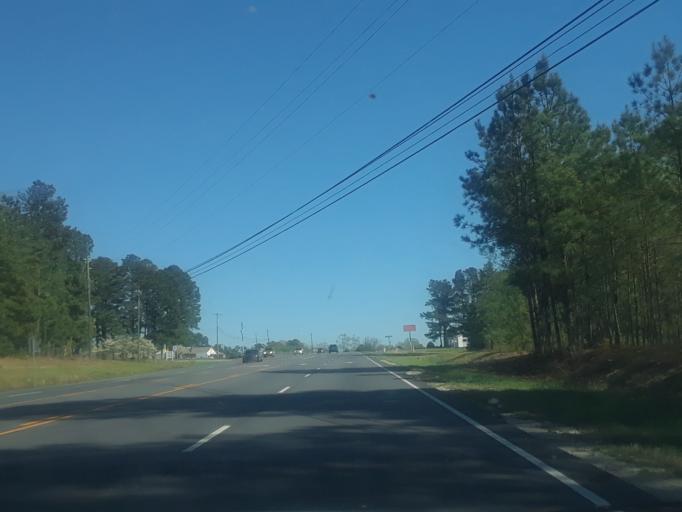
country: US
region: North Carolina
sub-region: Harnett County
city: Buies Creek
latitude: 35.3811
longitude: -78.7170
